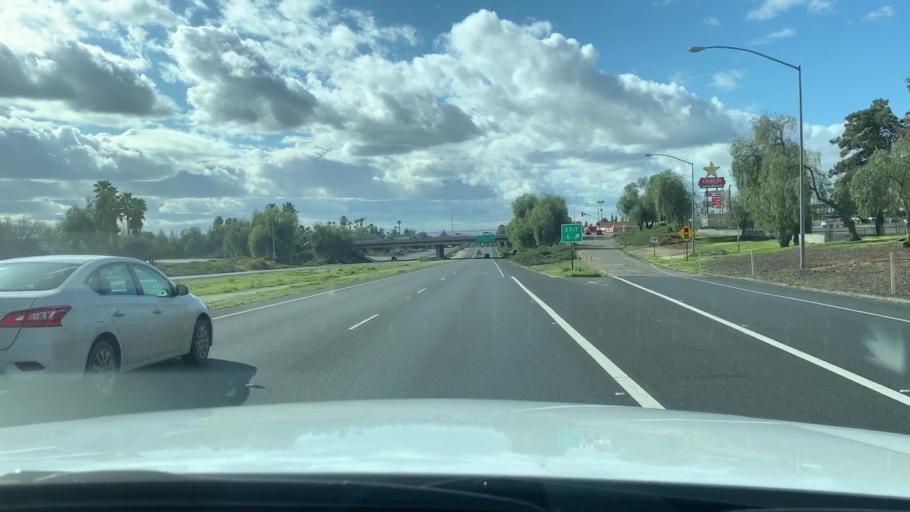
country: US
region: California
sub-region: Kern County
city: Bakersfield
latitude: 35.3966
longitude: -118.9470
